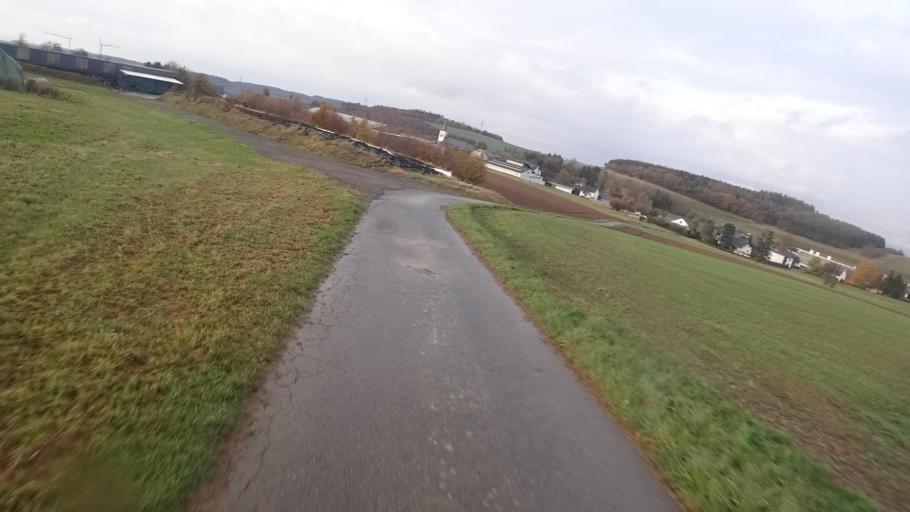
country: DE
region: Rheinland-Pfalz
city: Bickenbach
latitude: 50.1217
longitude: 7.5273
